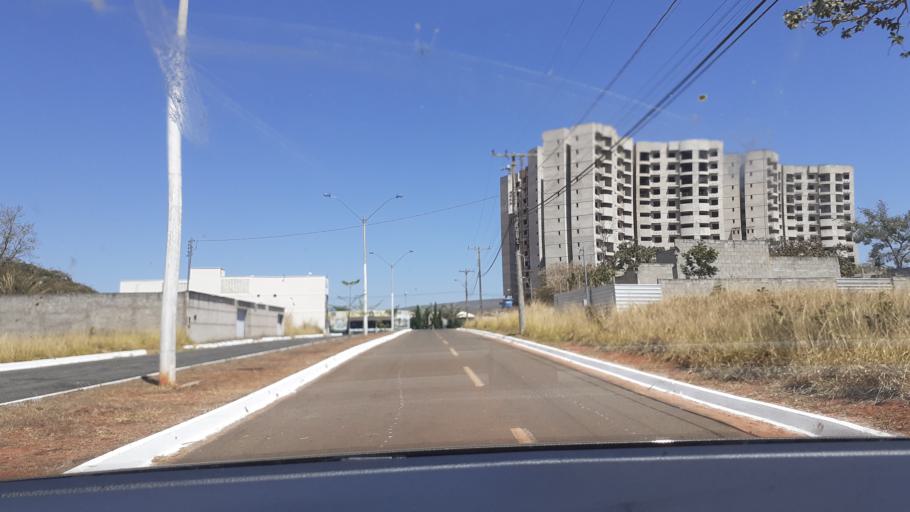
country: BR
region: Goias
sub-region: Caldas Novas
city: Caldas Novas
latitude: -17.7399
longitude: -48.6361
